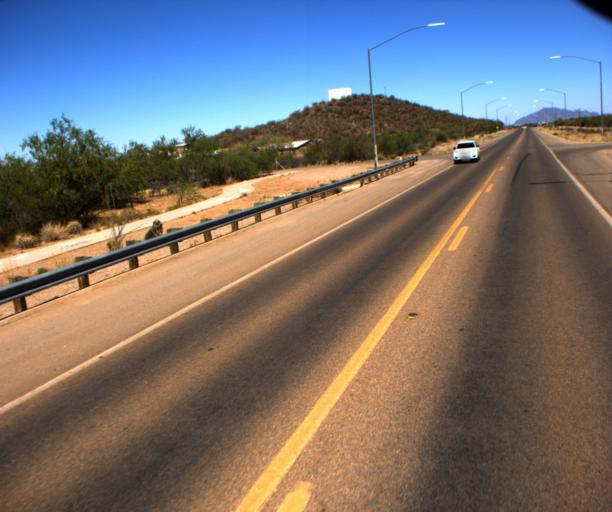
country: US
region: Arizona
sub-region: Pima County
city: Sells
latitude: 31.9194
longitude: -111.8832
